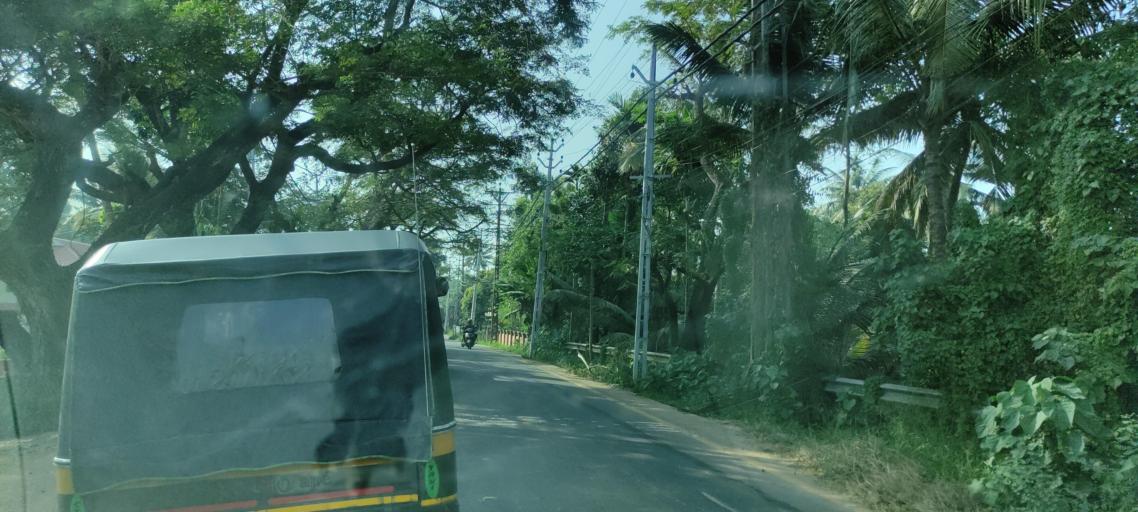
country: IN
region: Kerala
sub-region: Kottayam
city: Changanacheri
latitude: 9.3614
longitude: 76.4707
